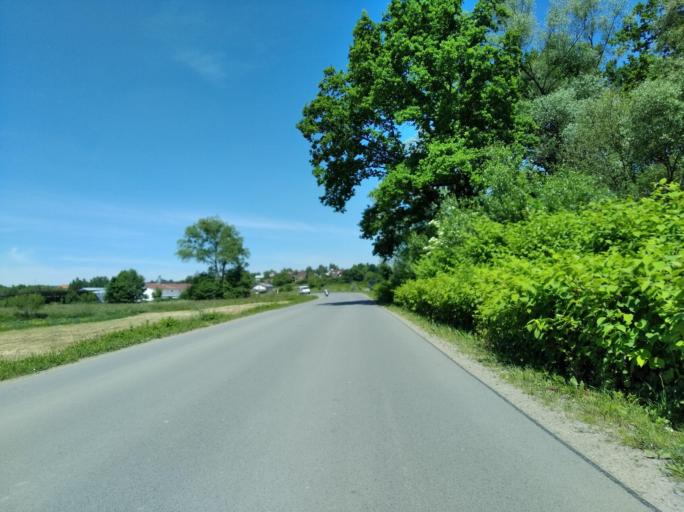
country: PL
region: Subcarpathian Voivodeship
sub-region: Powiat jasielski
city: Tarnowiec
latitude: 49.7487
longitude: 21.5903
